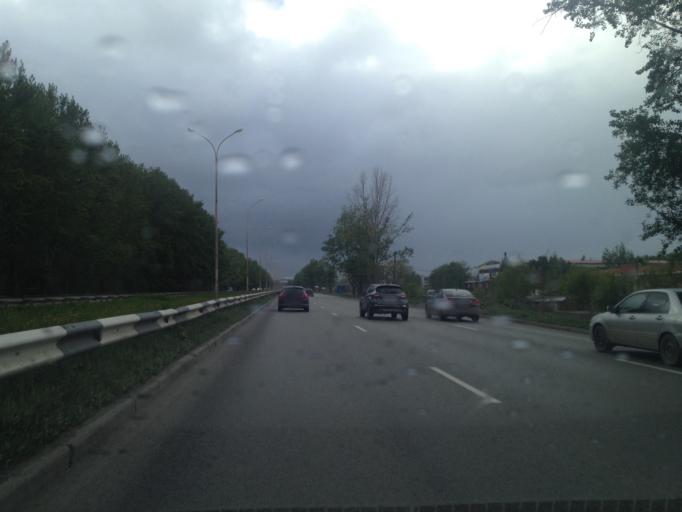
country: RU
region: Sverdlovsk
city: Sovkhoznyy
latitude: 56.7952
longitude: 60.5637
